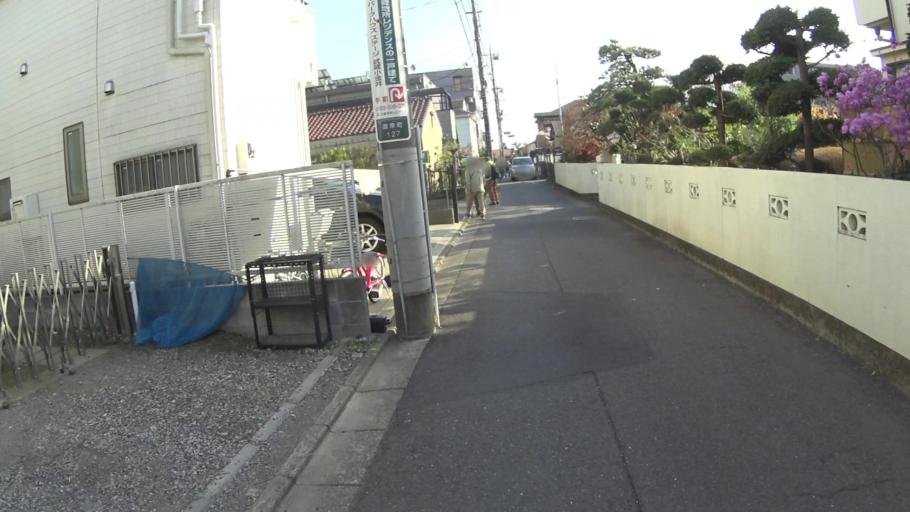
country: JP
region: Tokyo
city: Kokubunji
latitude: 35.7132
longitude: 139.5021
